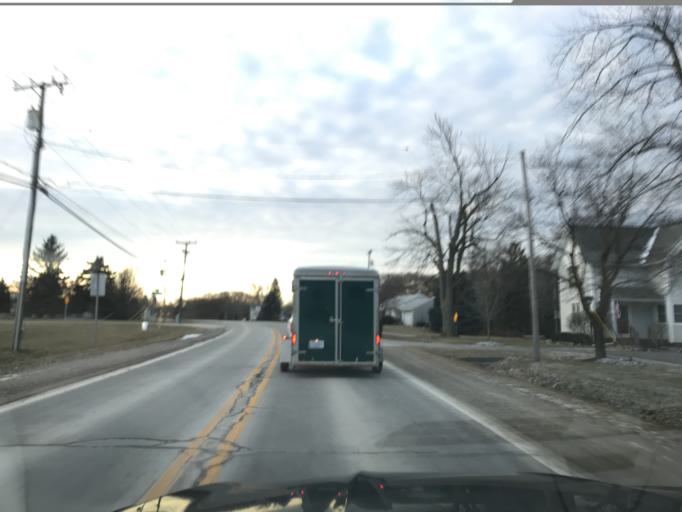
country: US
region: Michigan
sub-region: Macomb County
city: Armada
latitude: 42.8658
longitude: -82.8853
